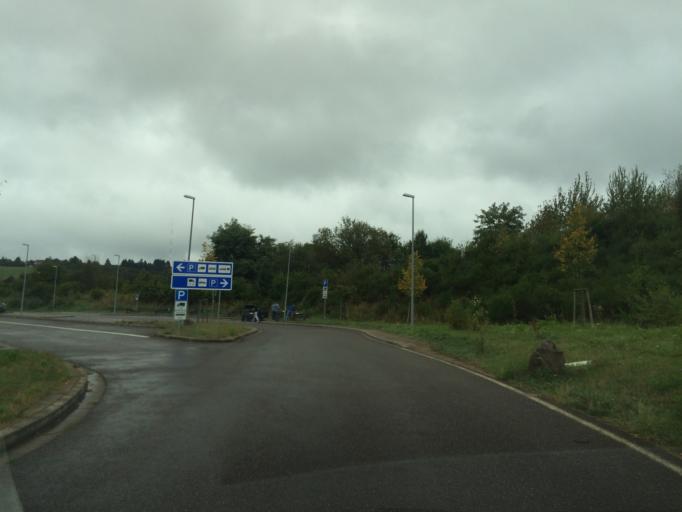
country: DE
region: Saarland
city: Eppelborn
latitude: 49.3505
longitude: 6.9933
